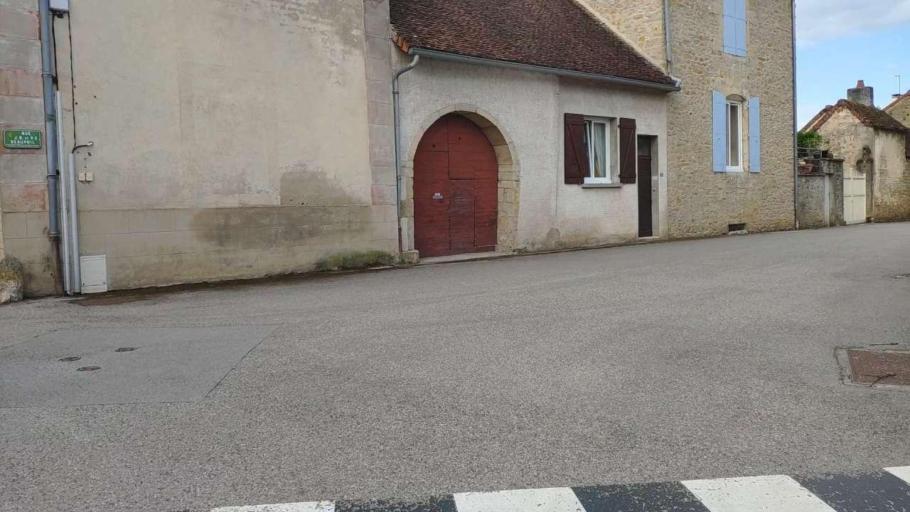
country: FR
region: Franche-Comte
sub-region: Departement du Jura
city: Perrigny
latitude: 46.7659
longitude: 5.5979
